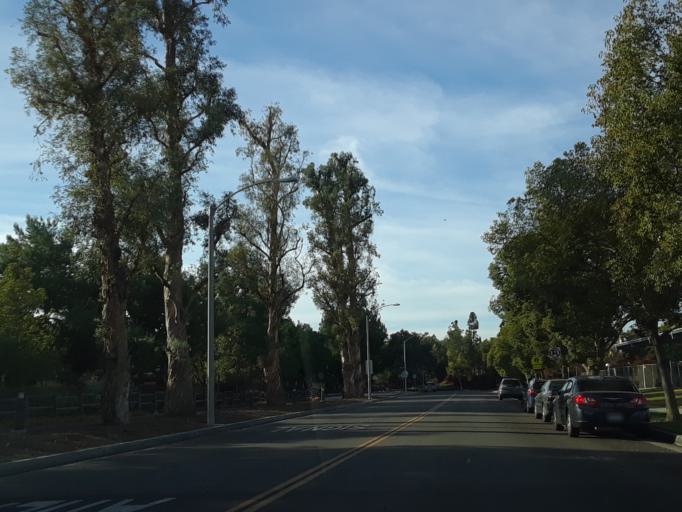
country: US
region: California
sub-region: Orange County
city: North Tustin
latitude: 33.7272
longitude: -117.7723
